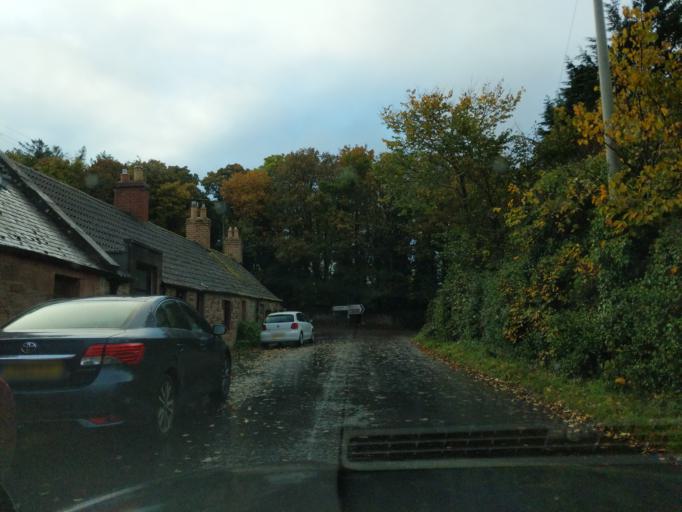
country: GB
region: Scotland
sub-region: East Lothian
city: Dunbar
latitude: 55.9568
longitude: -2.4622
